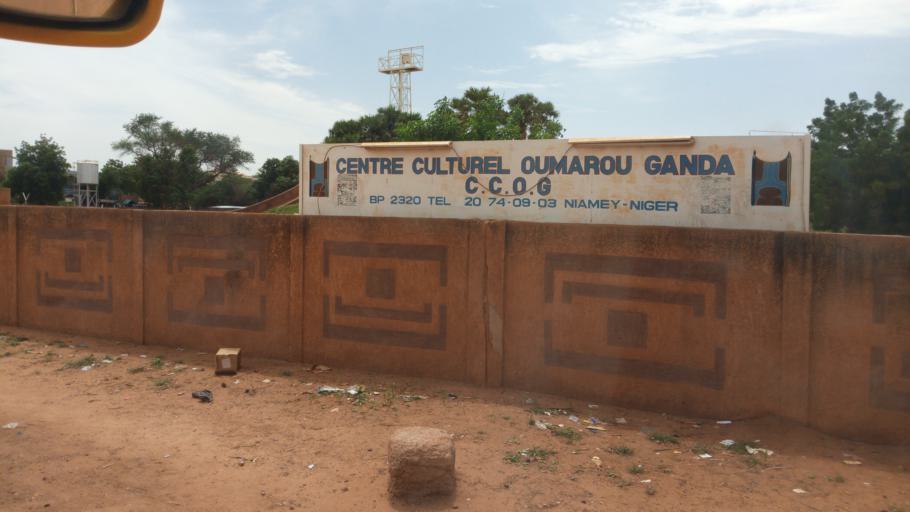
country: NE
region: Niamey
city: Niamey
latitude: 13.5221
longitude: 2.1363
